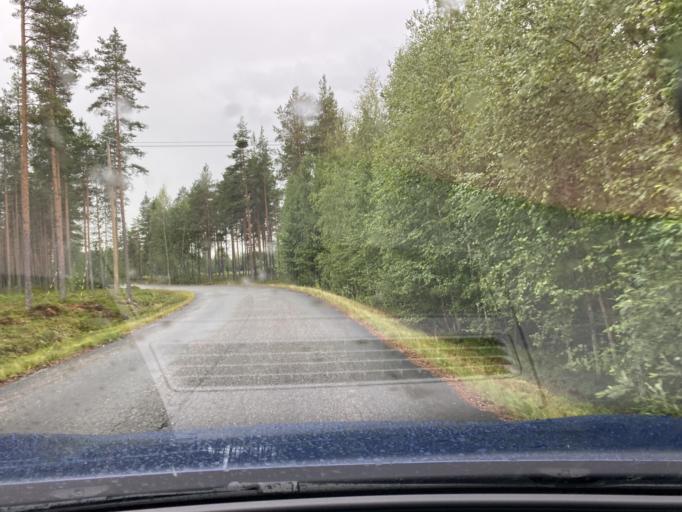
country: FI
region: Central Ostrobothnia
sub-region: Kaustinen
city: Halsua
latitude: 63.4139
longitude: 23.9757
